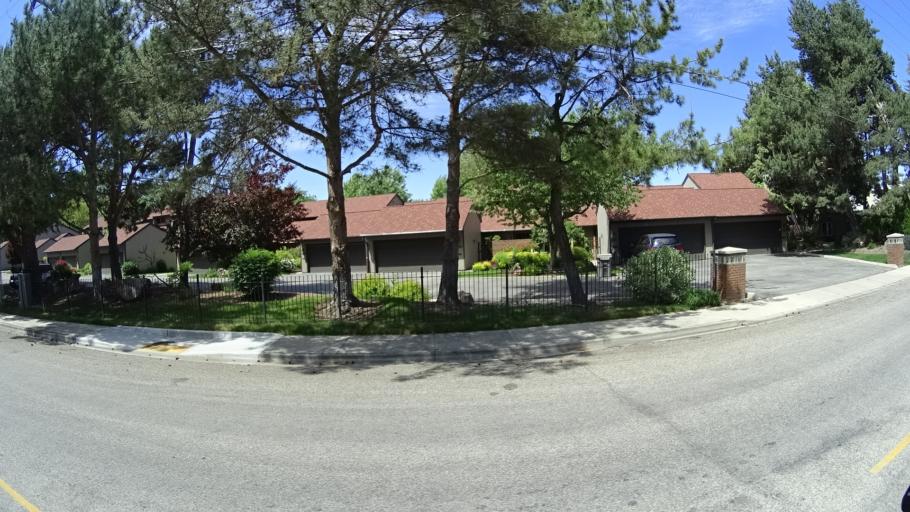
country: US
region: Idaho
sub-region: Ada County
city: Garden City
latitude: 43.5851
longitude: -116.2336
